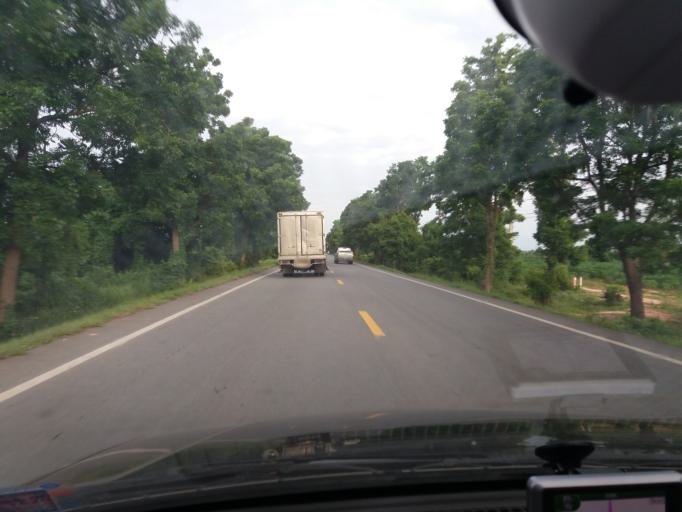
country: TH
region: Kanchanaburi
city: Huai Krachao
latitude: 14.3324
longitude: 99.7406
